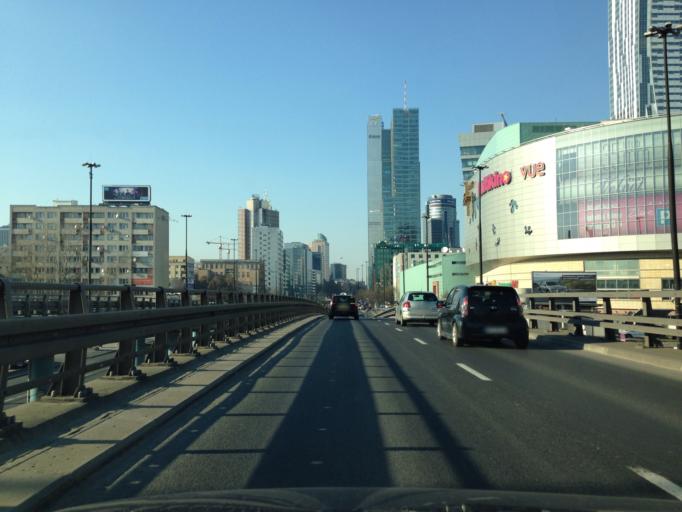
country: PL
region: Masovian Voivodeship
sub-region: Warszawa
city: Warsaw
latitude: 52.2281
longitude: 21.0018
